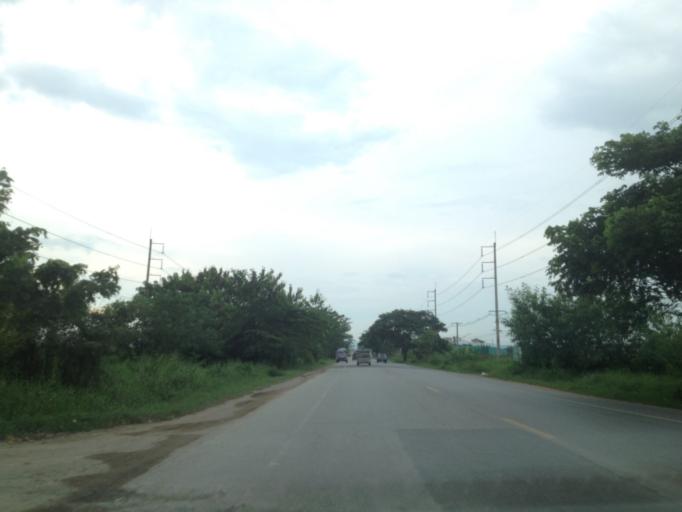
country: TH
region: Chiang Mai
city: Saraphi
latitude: 18.7200
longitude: 98.9970
